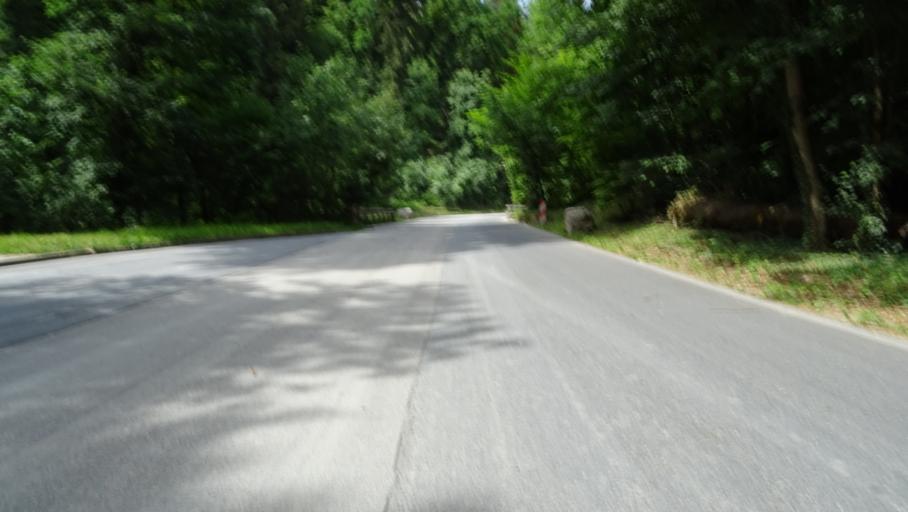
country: DE
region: Baden-Wuerttemberg
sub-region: Regierungsbezirk Stuttgart
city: Gundelsheim
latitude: 49.2914
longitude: 9.1606
